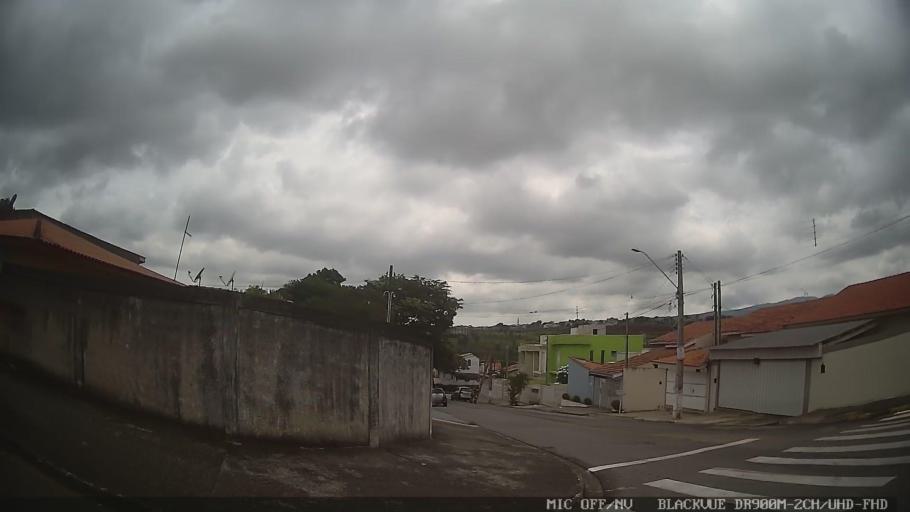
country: BR
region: Sao Paulo
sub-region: Atibaia
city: Atibaia
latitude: -23.1316
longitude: -46.5829
